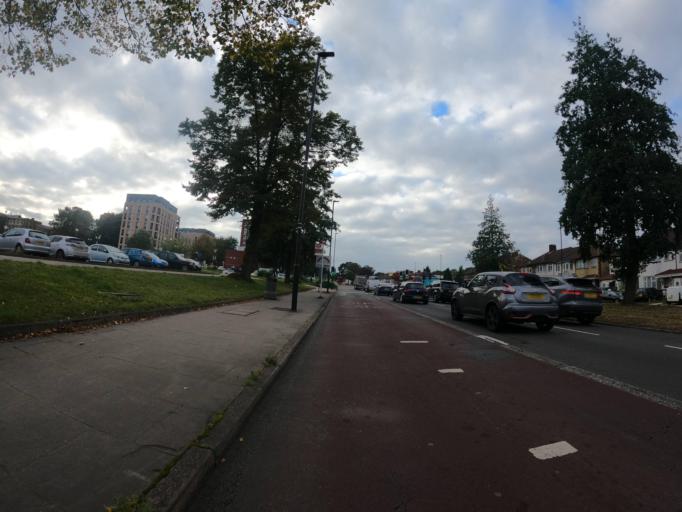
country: GB
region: England
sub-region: Greater London
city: Greenford
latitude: 51.5086
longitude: -0.3457
